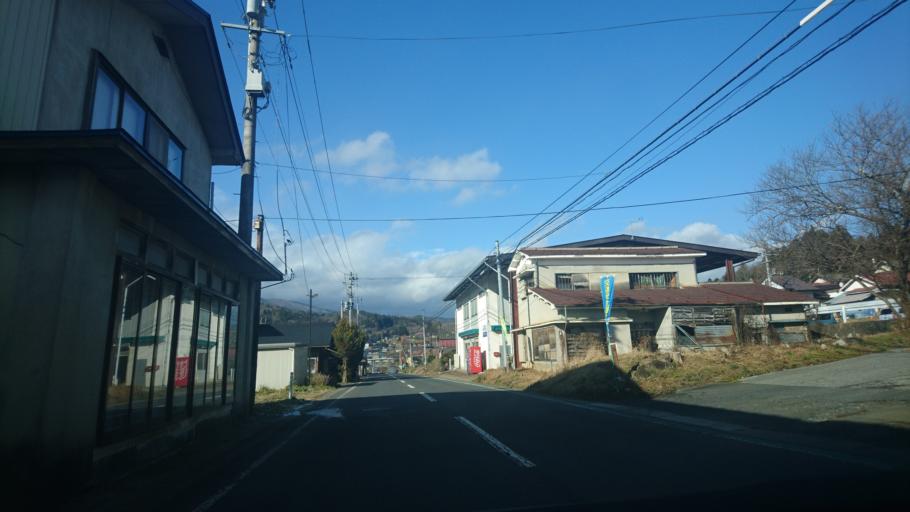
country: JP
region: Iwate
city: Mizusawa
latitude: 39.0441
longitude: 141.3691
